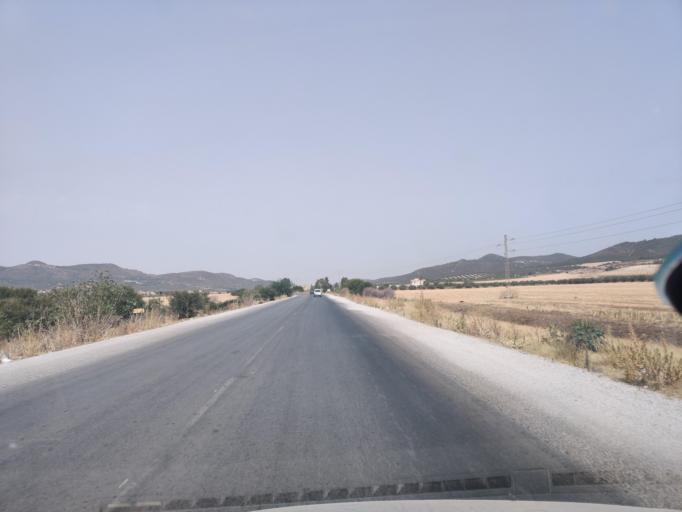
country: TN
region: Tunis
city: Hammam-Lif
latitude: 36.6170
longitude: 10.4176
